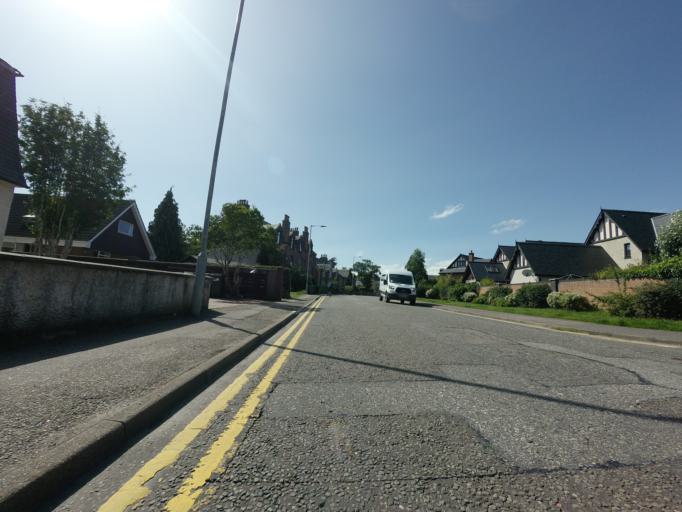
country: GB
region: Scotland
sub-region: Highland
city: Inverness
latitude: 57.4749
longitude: -4.2139
